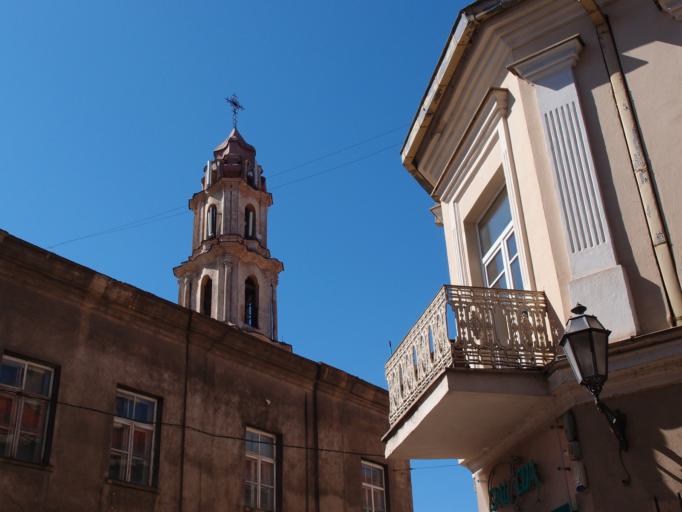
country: LT
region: Vilnius County
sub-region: Vilnius
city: Vilnius
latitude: 54.6795
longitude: 25.2908
